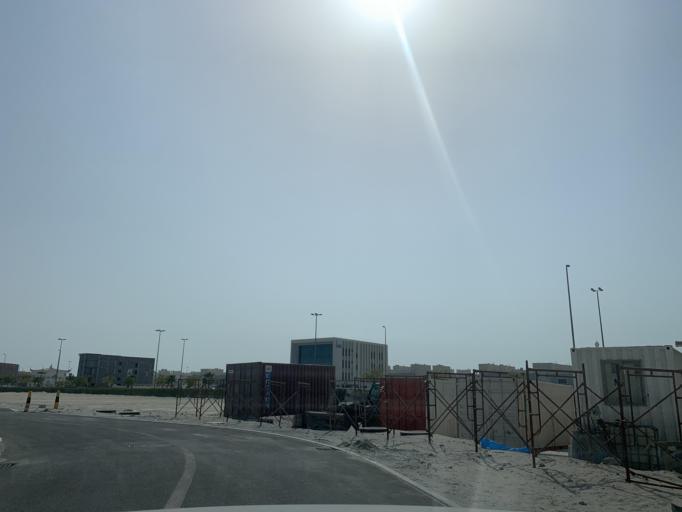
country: BH
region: Muharraq
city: Al Muharraq
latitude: 26.3088
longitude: 50.6313
